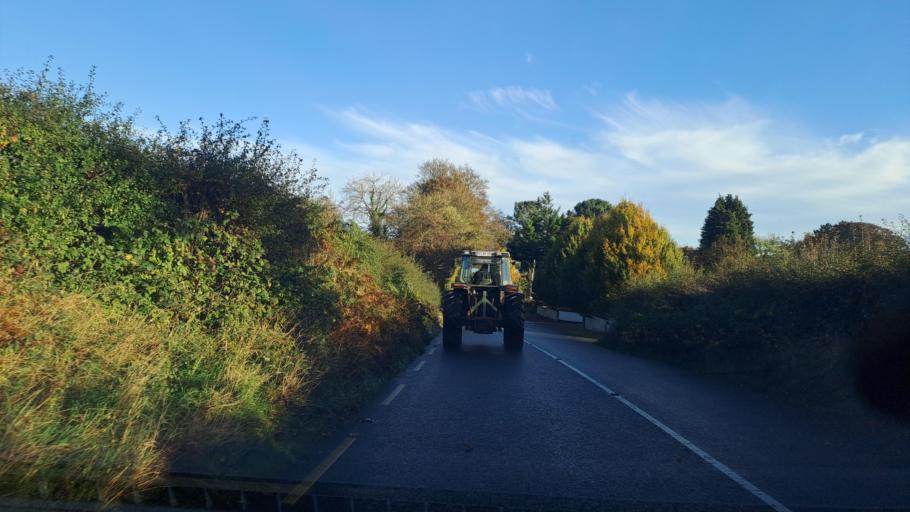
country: IE
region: Ulster
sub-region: County Monaghan
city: Monaghan
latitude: 54.2236
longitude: -6.9734
